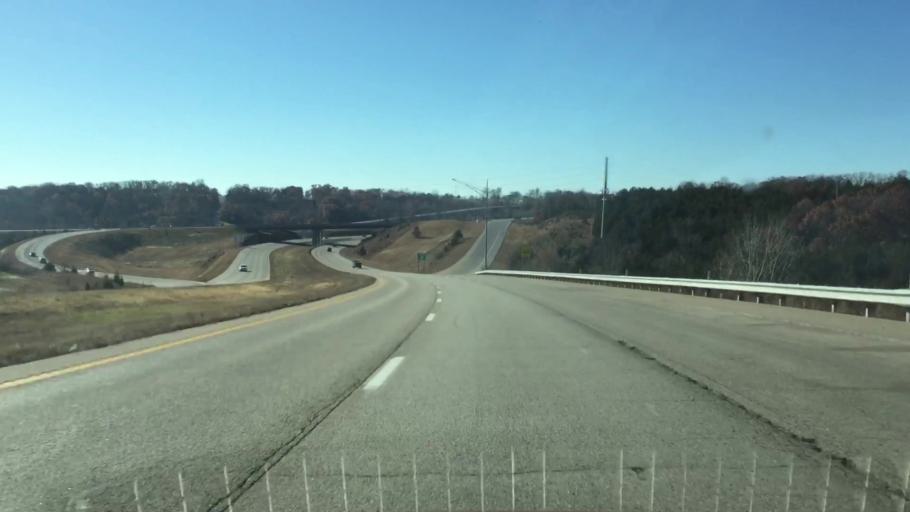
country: US
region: Missouri
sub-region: Cole County
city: Jefferson City
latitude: 38.5446
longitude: -92.2082
